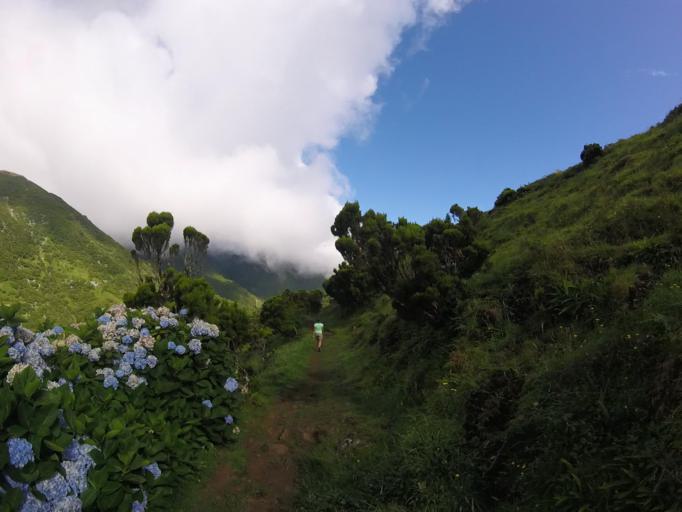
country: PT
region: Azores
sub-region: Sao Roque do Pico
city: Sao Roque do Pico
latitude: 38.6027
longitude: -27.9208
